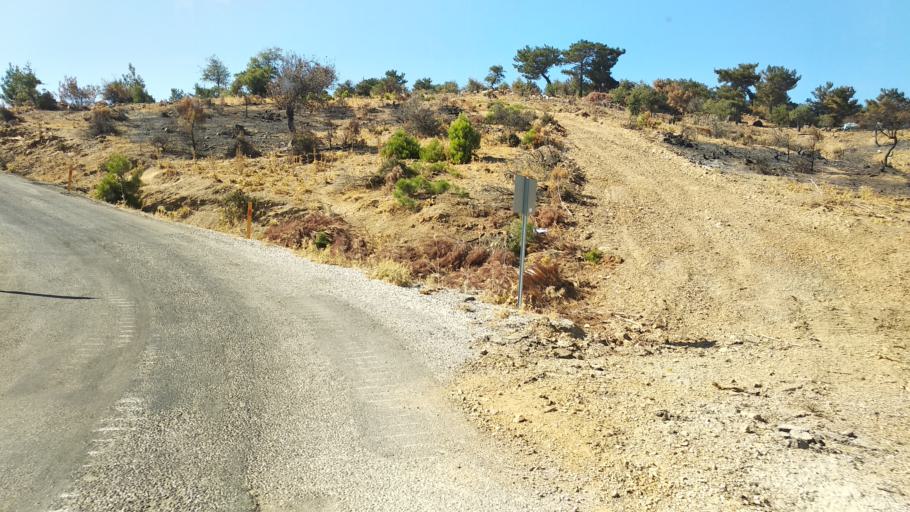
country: TR
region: Izmir
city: Gaziemir
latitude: 38.2949
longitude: 27.0017
